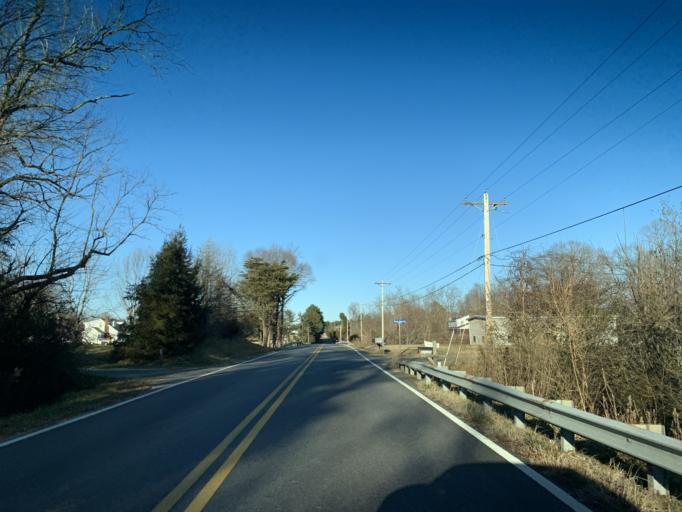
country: US
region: Maryland
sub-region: Saint Mary's County
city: Mechanicsville
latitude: 38.4238
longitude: -76.6905
